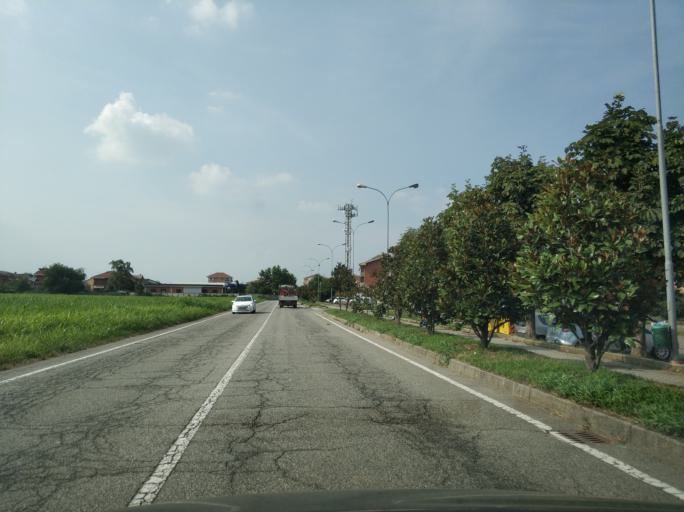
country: IT
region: Piedmont
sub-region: Provincia di Torino
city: Leini
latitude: 45.1784
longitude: 7.7094
